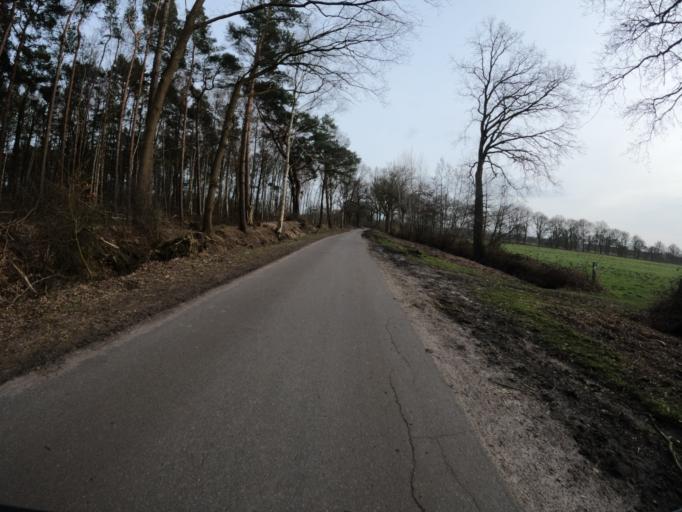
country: DE
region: Schleswig-Holstein
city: Rellingen
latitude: 53.6051
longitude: 9.7892
